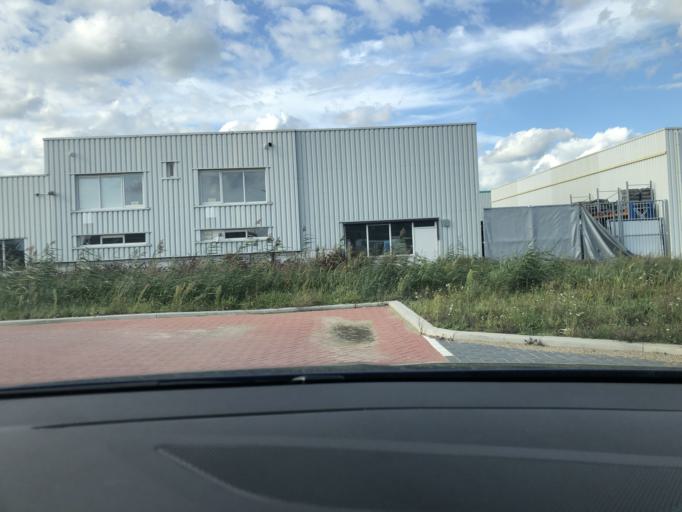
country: NL
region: South Holland
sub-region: Gemeente Lansingerland
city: Bleiswijk
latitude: 52.0070
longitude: 4.5907
